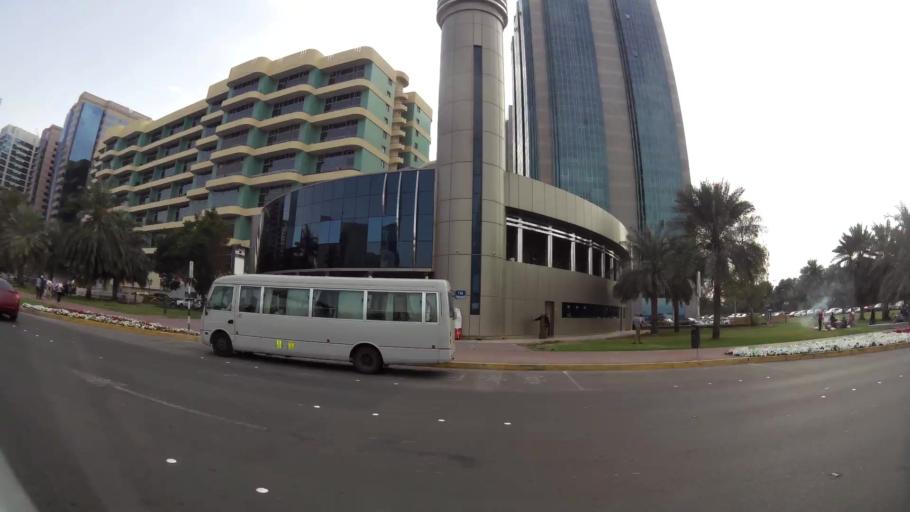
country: AE
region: Abu Dhabi
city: Abu Dhabi
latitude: 24.4769
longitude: 54.3467
